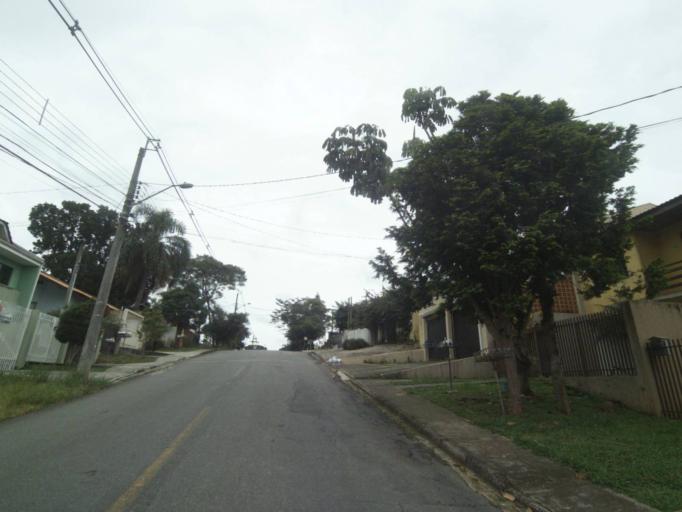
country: BR
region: Parana
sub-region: Curitiba
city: Curitiba
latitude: -25.4436
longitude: -49.3286
